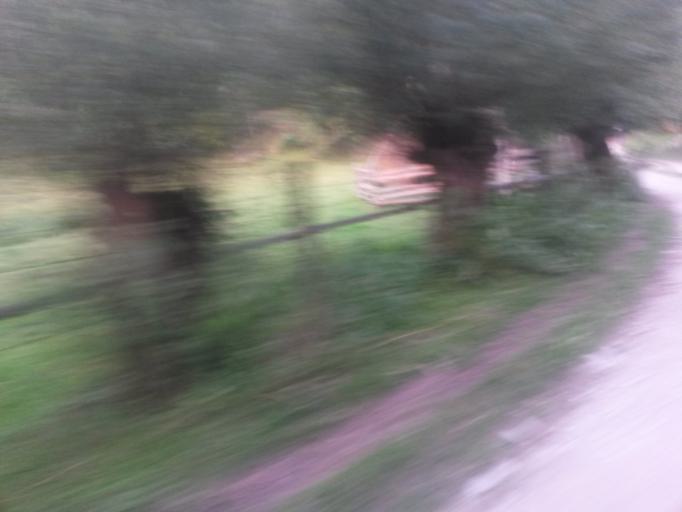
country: RO
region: Alba
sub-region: Comuna Ponor
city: Ponor
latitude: 46.3101
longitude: 23.4083
